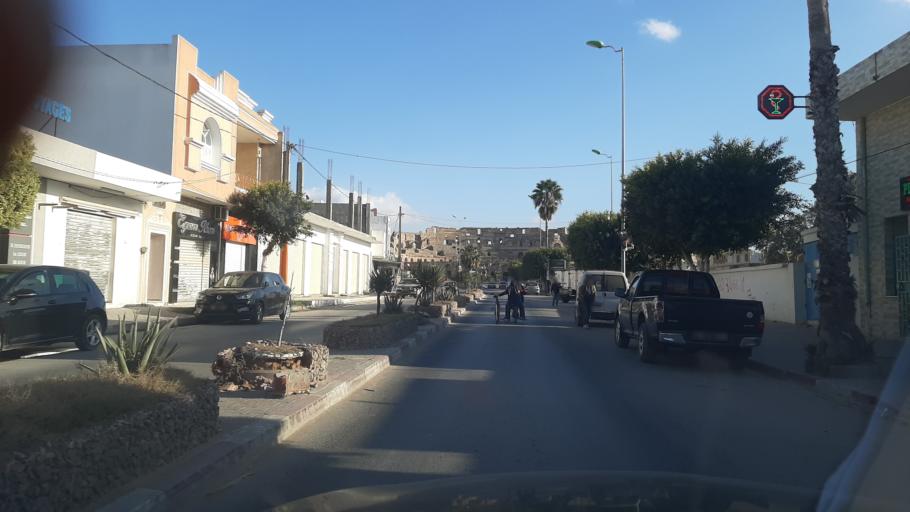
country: TN
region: Al Mahdiyah
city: El Jem
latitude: 35.2990
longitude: 10.7053
